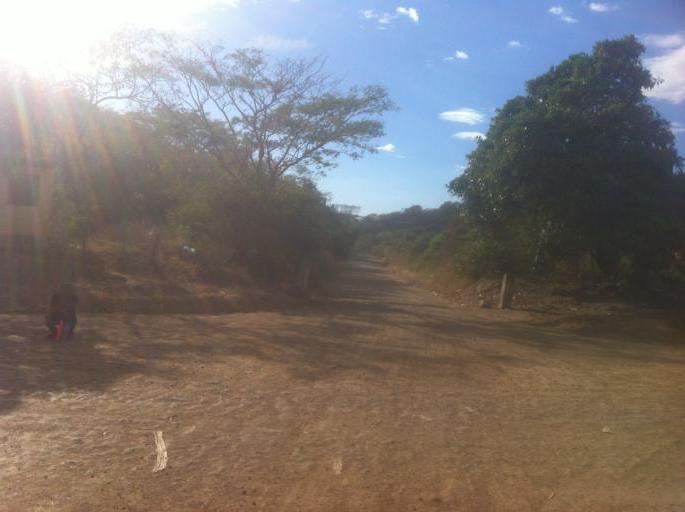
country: NI
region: Managua
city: Masachapa
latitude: 11.8114
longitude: -86.4945
